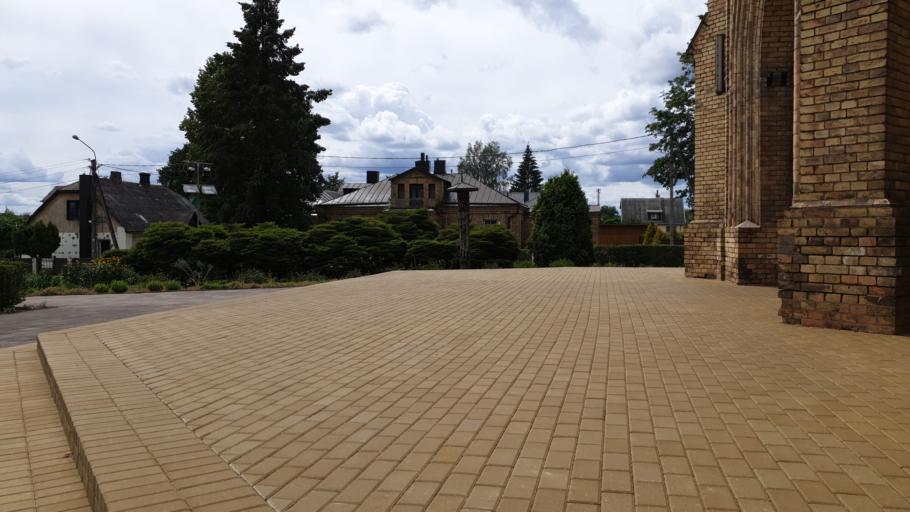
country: LT
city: Skaidiskes
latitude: 54.6971
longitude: 25.4110
